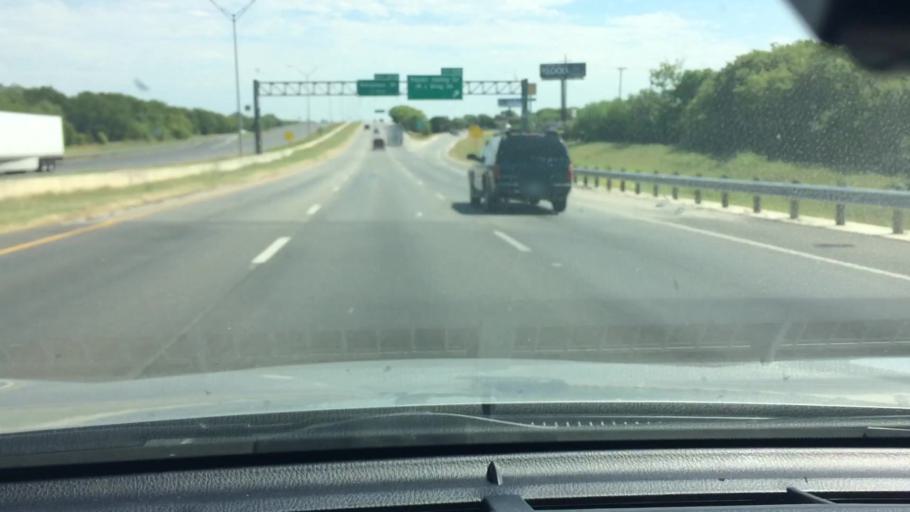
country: US
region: Texas
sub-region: Bexar County
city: San Antonio
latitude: 29.4091
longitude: -98.4406
